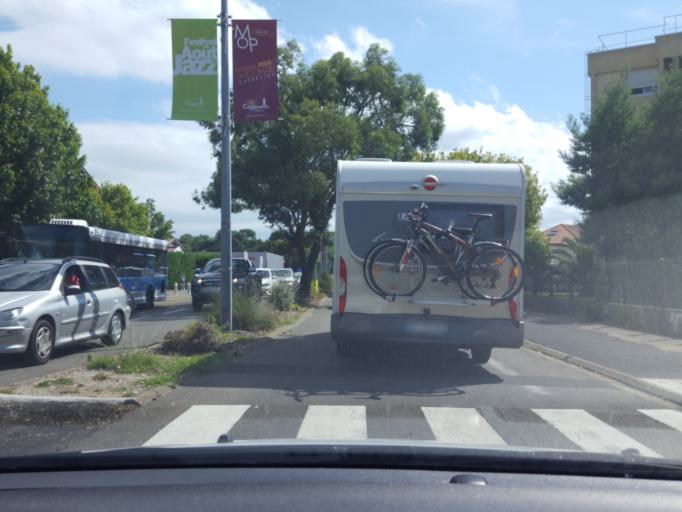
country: FR
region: Aquitaine
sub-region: Departement des Landes
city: Capbreton
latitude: 43.6406
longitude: -1.4256
